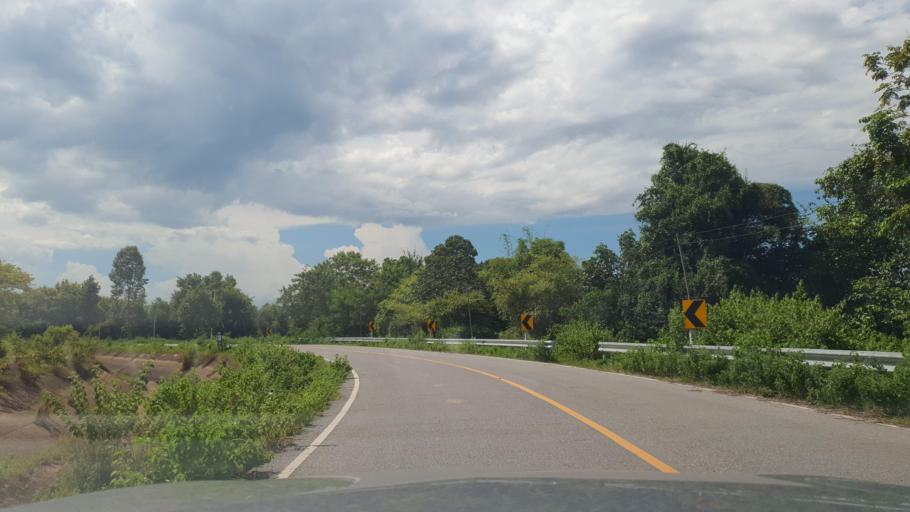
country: TH
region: Chiang Mai
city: Mae On
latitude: 18.7751
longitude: 99.1863
